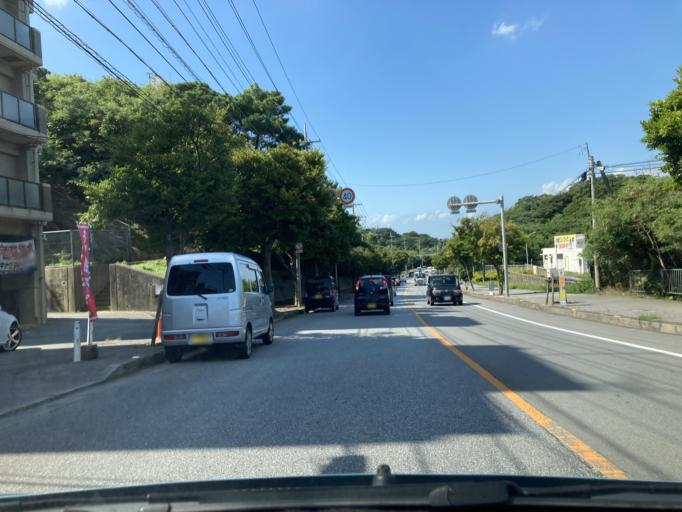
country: JP
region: Okinawa
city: Ginowan
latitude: 26.2453
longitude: 127.7608
